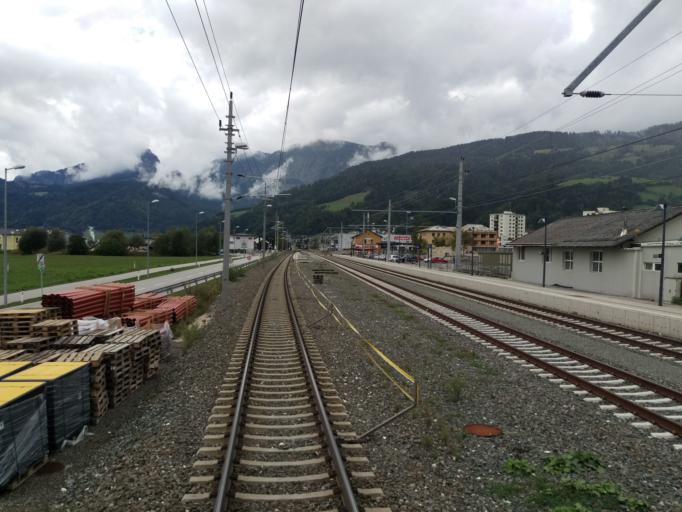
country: AT
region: Styria
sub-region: Politischer Bezirk Liezen
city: Liezen
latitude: 47.5614
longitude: 14.2445
